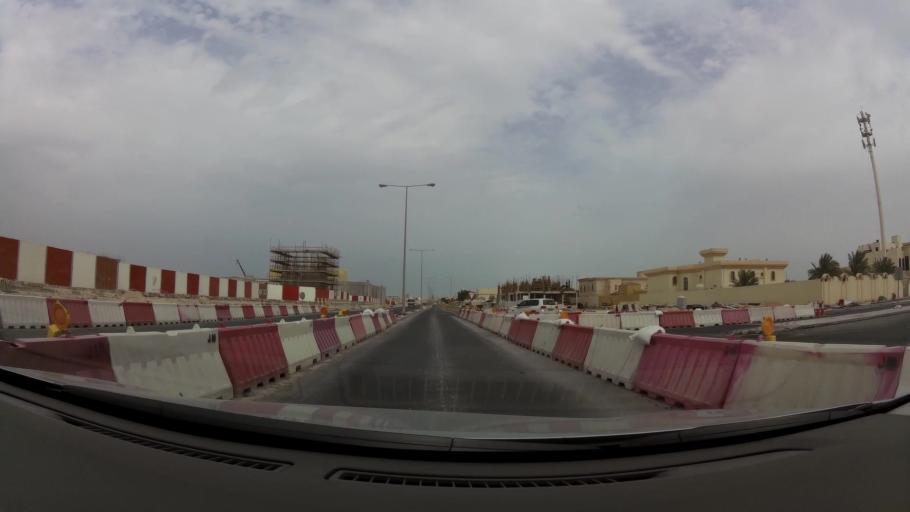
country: QA
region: Baladiyat ar Rayyan
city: Ar Rayyan
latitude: 25.3546
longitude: 51.4649
